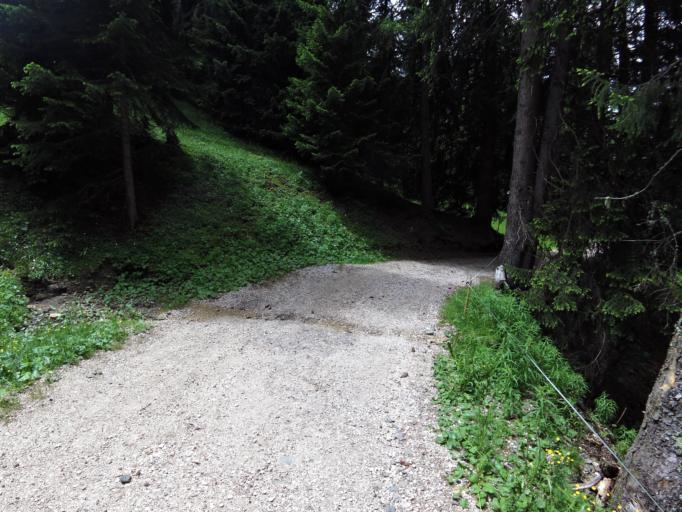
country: IT
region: Trentino-Alto Adige
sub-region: Bolzano
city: Ortisei
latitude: 46.5298
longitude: 11.6477
